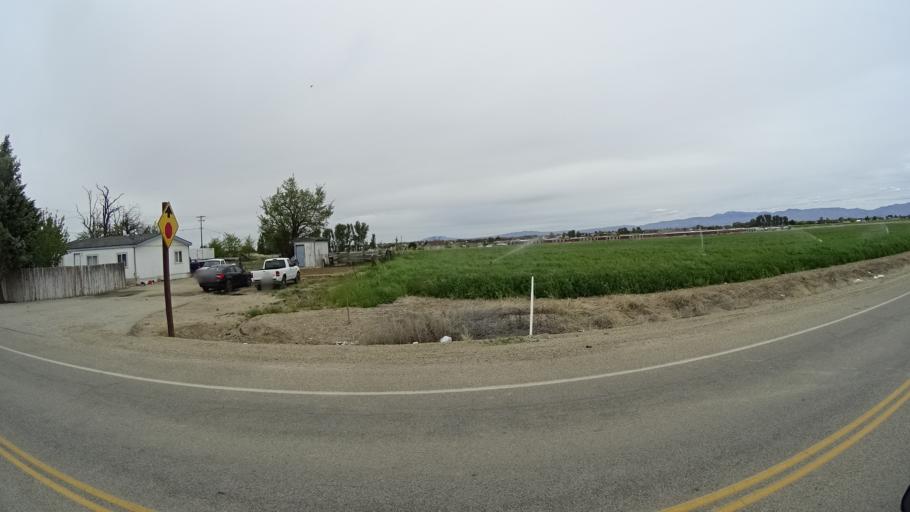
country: US
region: Idaho
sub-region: Ada County
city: Kuna
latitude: 43.4879
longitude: -116.3938
